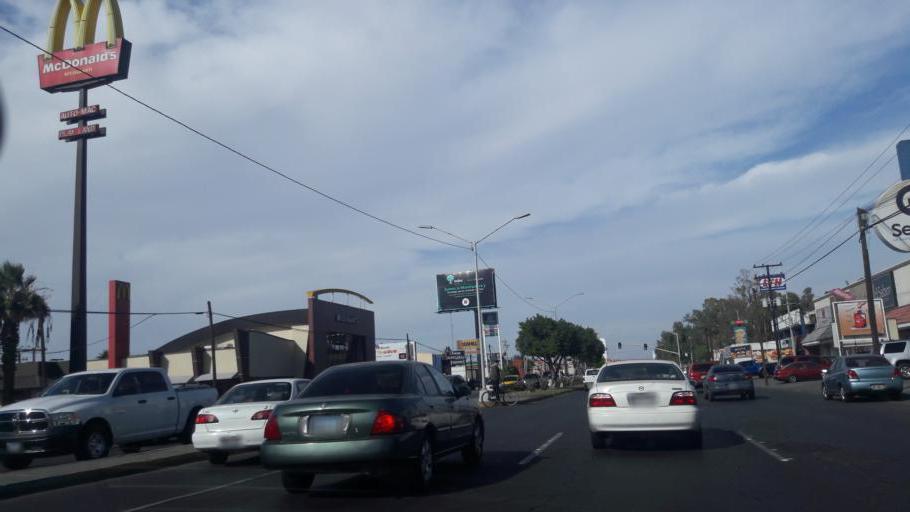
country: MX
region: Baja California
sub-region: Mexicali
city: Mexicali
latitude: 32.6291
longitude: -115.4453
